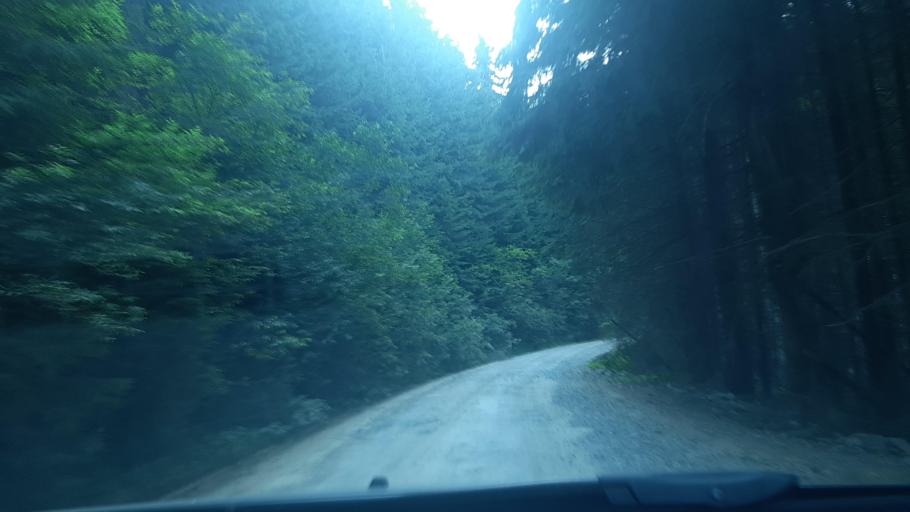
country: RO
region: Alba
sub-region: Comuna Sugag
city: Sugag
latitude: 45.5850
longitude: 23.6115
